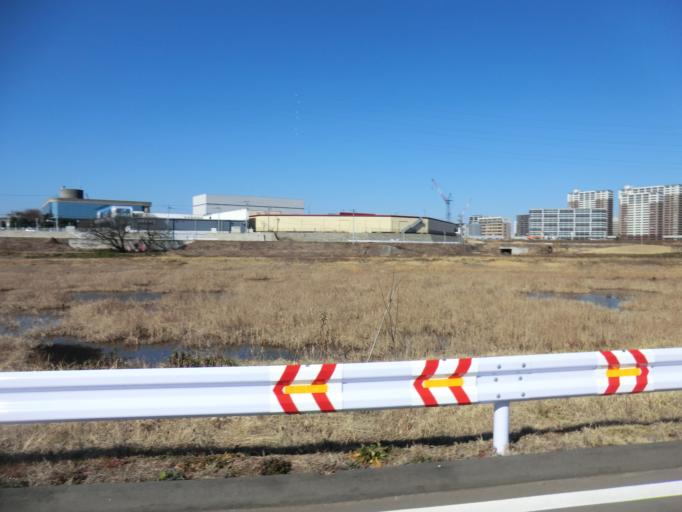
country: JP
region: Ibaraki
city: Naka
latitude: 36.0758
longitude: 140.0882
